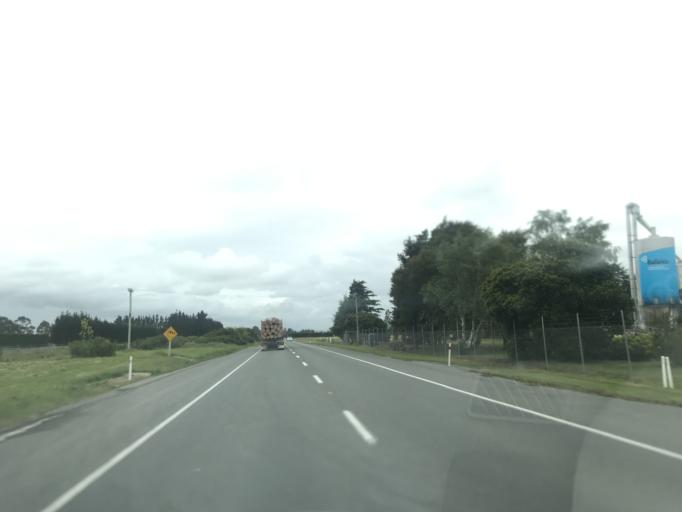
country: NZ
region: Canterbury
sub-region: Ashburton District
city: Tinwald
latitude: -43.9581
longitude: 171.6502
